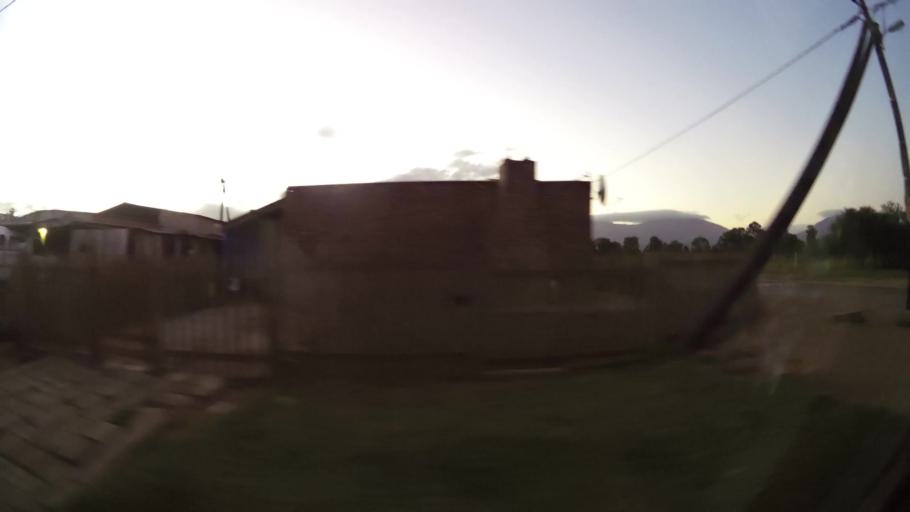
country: ZA
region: Western Cape
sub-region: Eden District Municipality
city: Riversdale
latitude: -34.1001
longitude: 21.2709
